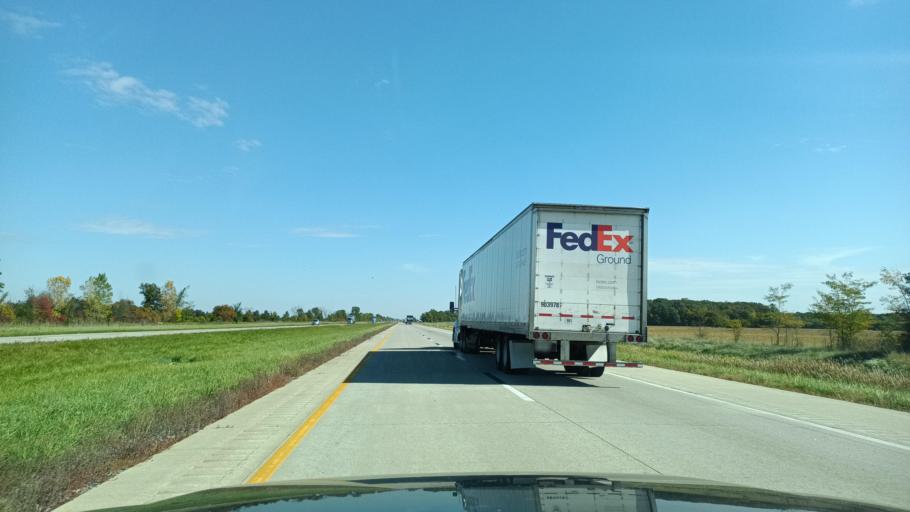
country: US
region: Ohio
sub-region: Paulding County
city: Antwerp
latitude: 41.1986
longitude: -84.6709
